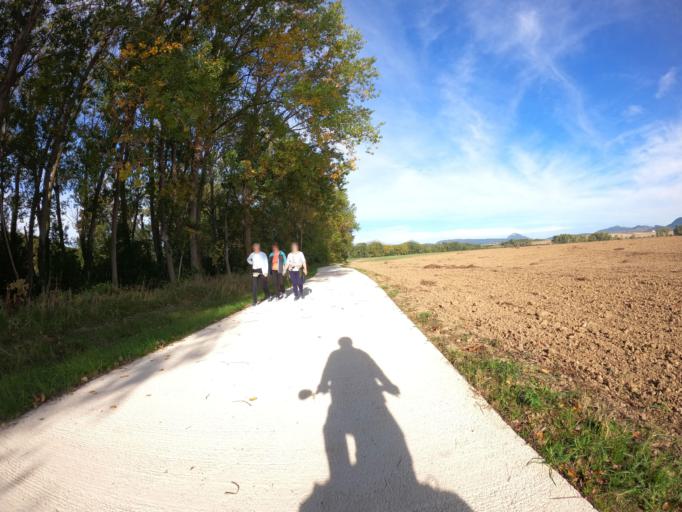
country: ES
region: Navarre
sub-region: Provincia de Navarra
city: Orkoien
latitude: 42.8107
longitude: -1.7340
